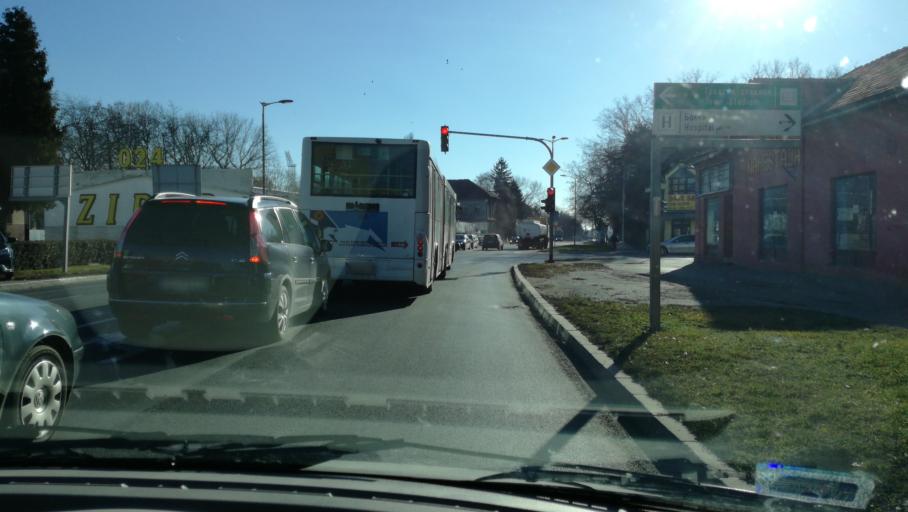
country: RS
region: Autonomna Pokrajina Vojvodina
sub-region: Severnobacki Okrug
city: Subotica
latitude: 46.0834
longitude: 19.6730
